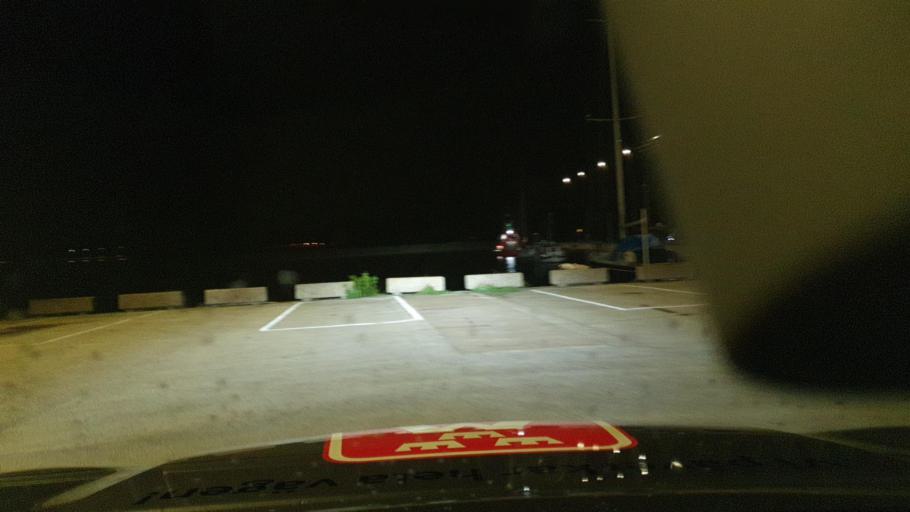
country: SE
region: Gotland
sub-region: Gotland
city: Slite
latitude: 57.8658
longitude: 19.0584
